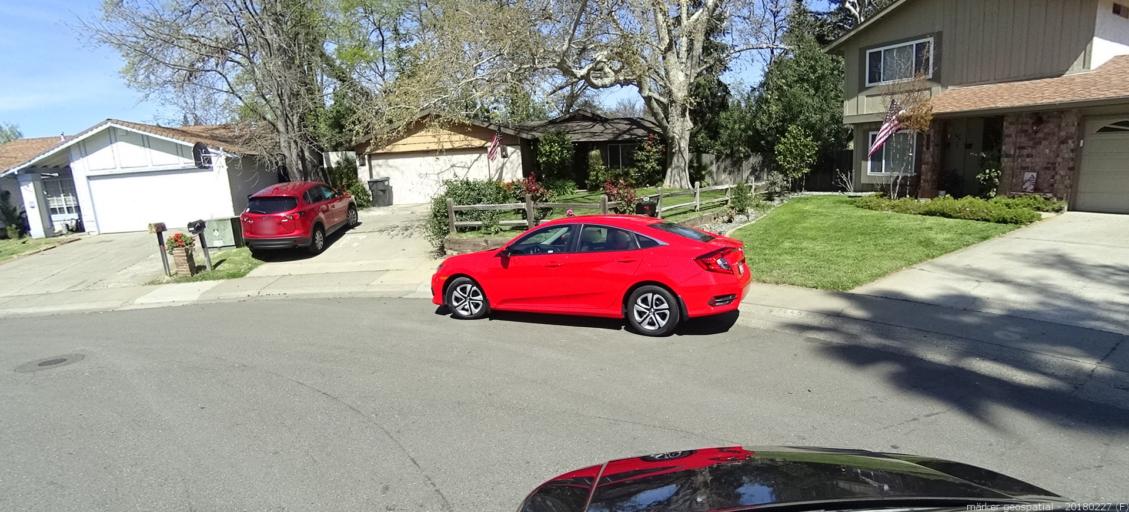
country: US
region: California
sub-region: Sacramento County
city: La Riviera
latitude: 38.5580
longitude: -121.3480
